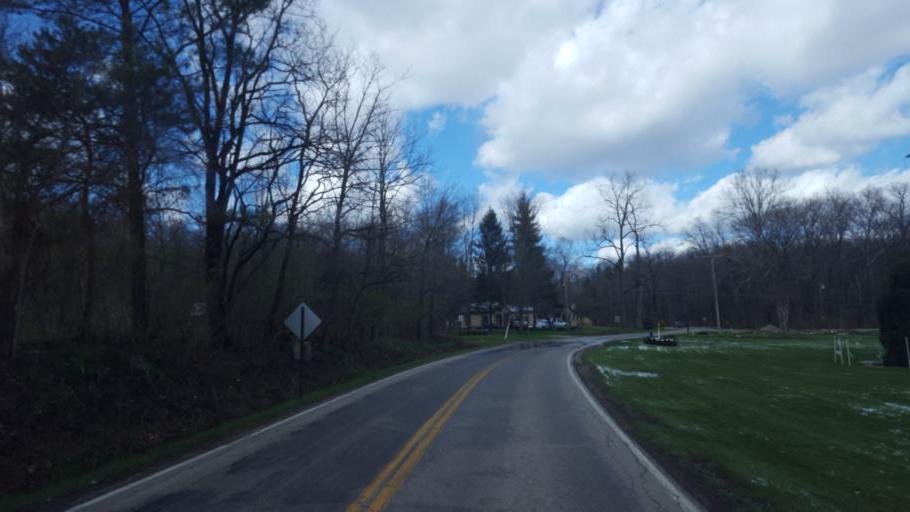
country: US
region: Ohio
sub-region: Richland County
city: Ontario
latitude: 40.7436
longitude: -82.6408
